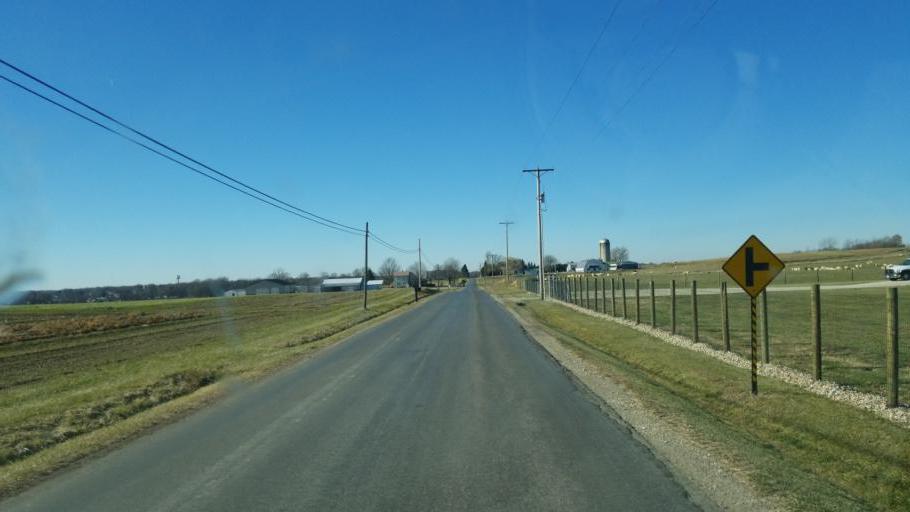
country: US
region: Ohio
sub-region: Huron County
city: Plymouth
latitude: 40.9747
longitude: -82.5828
